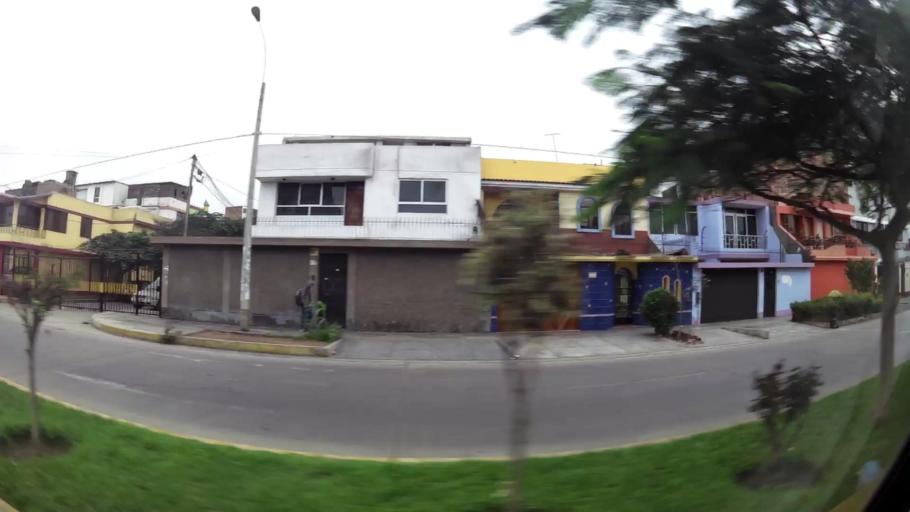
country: PE
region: Callao
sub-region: Callao
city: Callao
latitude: -12.0619
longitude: -77.0752
